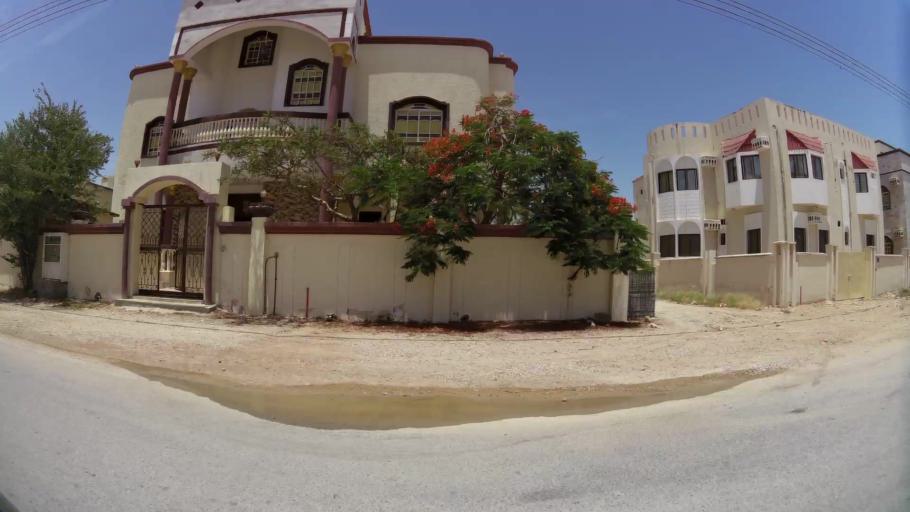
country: OM
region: Zufar
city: Salalah
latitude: 17.0700
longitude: 54.1546
